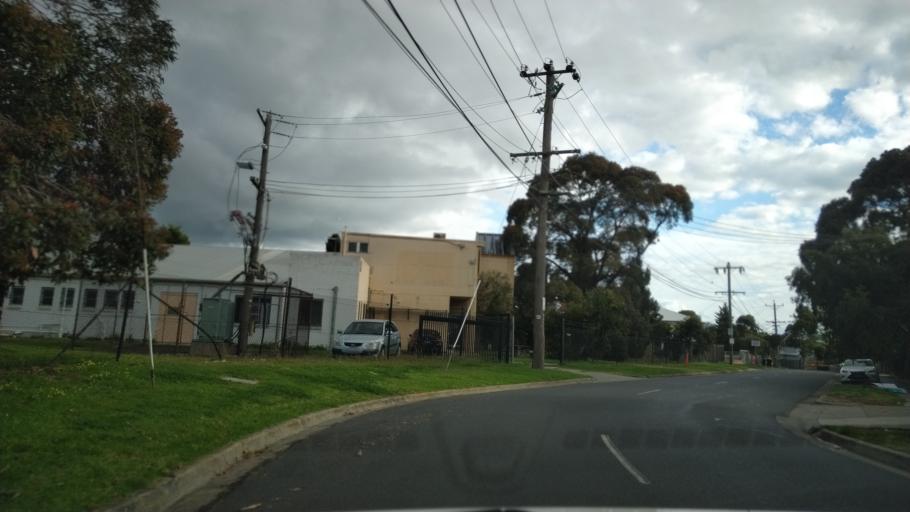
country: AU
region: Victoria
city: Highett
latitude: -37.9512
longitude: 145.0664
